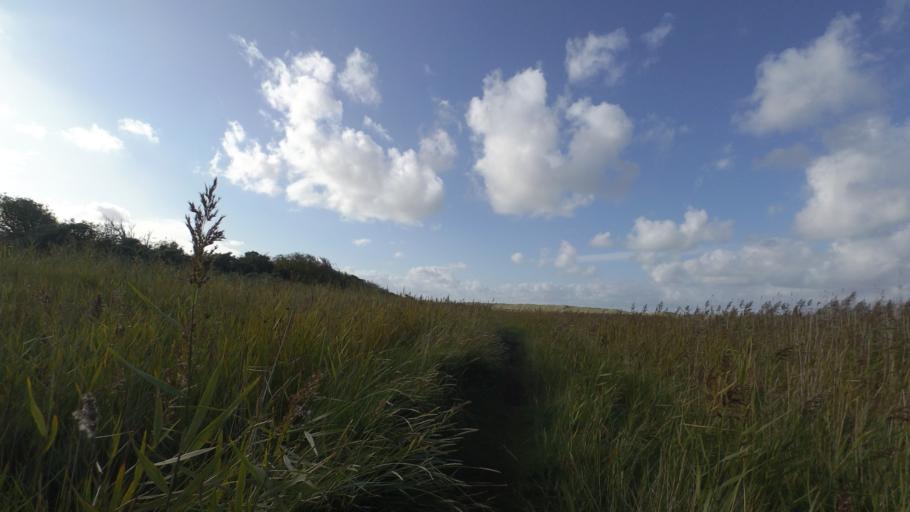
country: NL
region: Friesland
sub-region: Gemeente Dongeradeel
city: Ternaard
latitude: 53.4607
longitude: 5.9197
